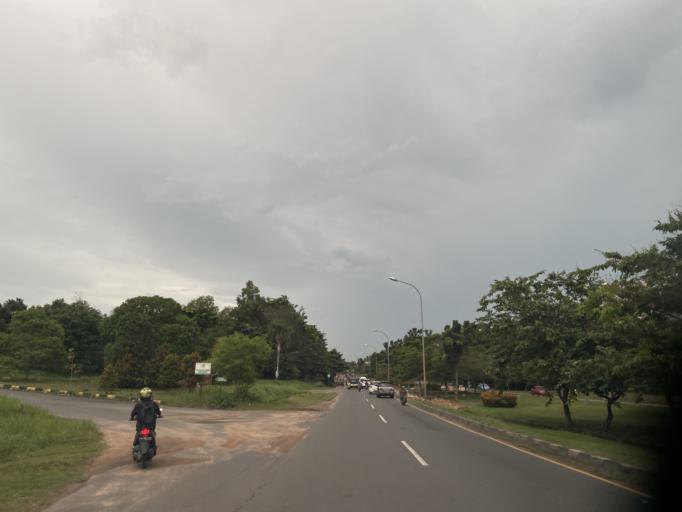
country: SG
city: Singapore
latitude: 1.0990
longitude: 104.0631
